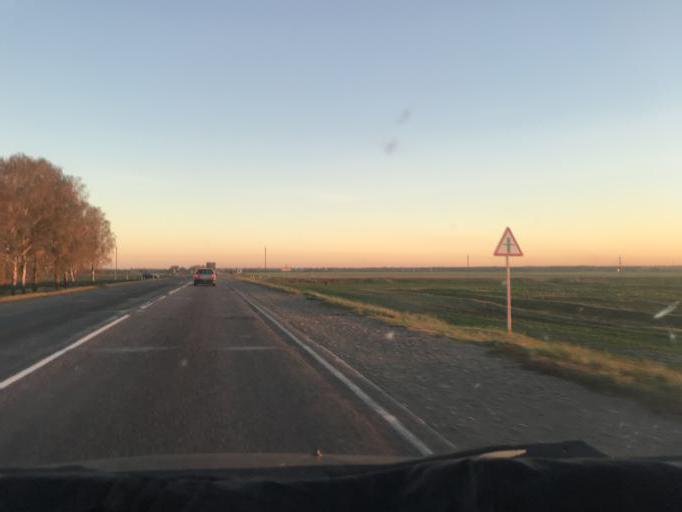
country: BY
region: Gomel
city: Kalinkavichy
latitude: 52.1507
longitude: 29.2464
